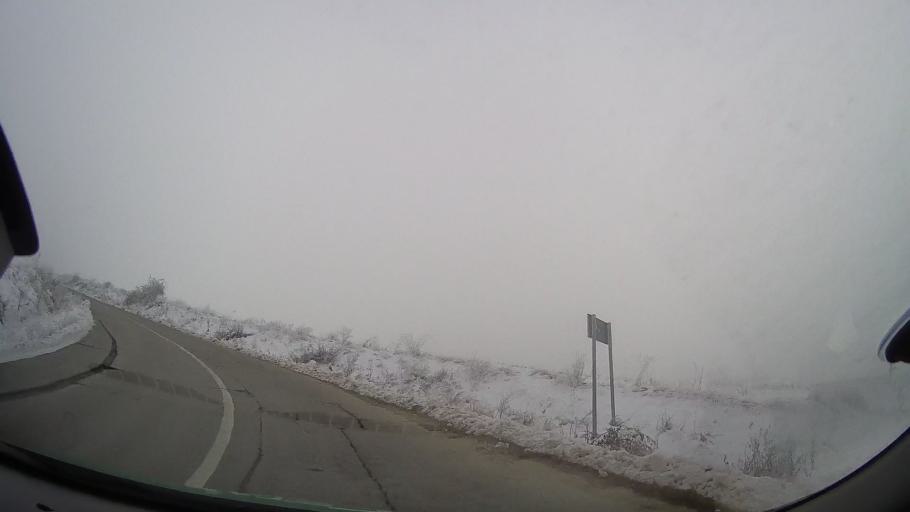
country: RO
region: Bacau
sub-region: Comuna Podu Turcului
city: Podu Turcului
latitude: 46.2087
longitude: 27.4198
